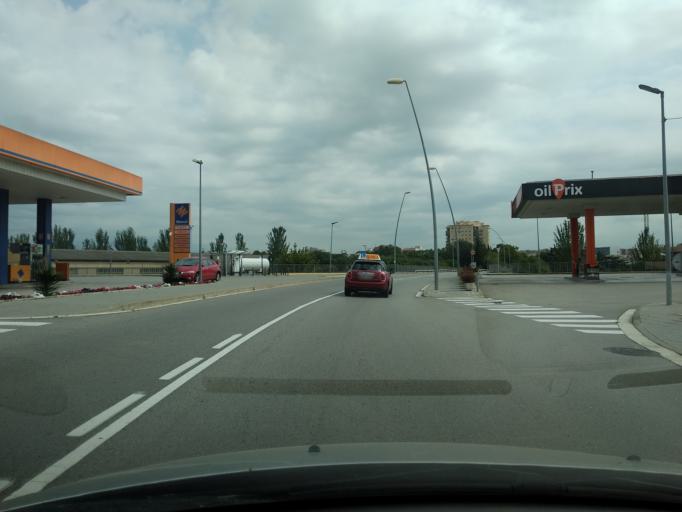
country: ES
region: Catalonia
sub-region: Provincia de Barcelona
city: Granollers
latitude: 41.6015
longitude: 2.2777
